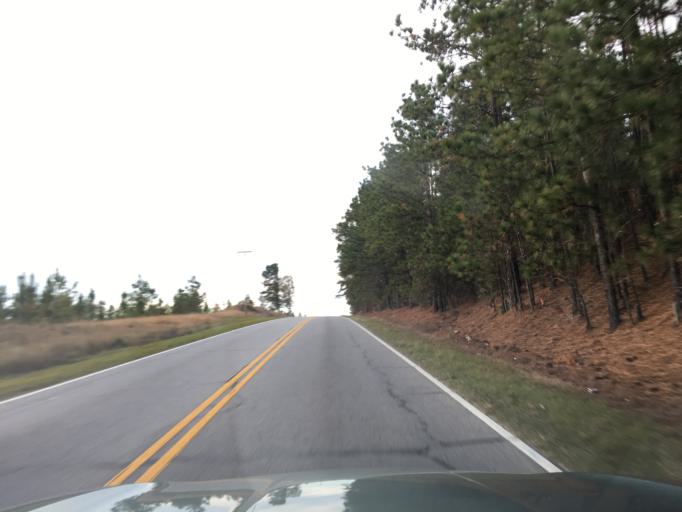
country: US
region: South Carolina
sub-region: Lexington County
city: Leesville
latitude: 33.8040
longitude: -81.4378
